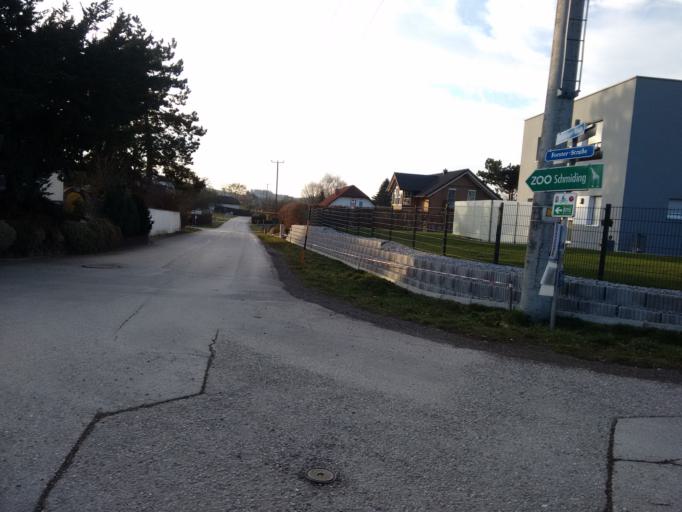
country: AT
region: Upper Austria
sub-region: Politischer Bezirk Grieskirchen
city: Bad Schallerbach
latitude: 48.1932
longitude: 13.9654
